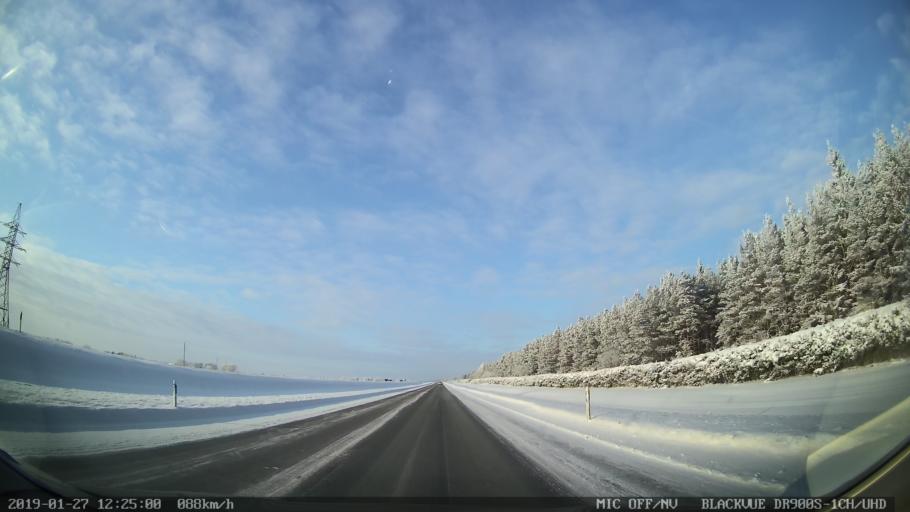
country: EE
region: Harju
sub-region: Raasiku vald
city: Arukula
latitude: 59.4450
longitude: 25.1077
